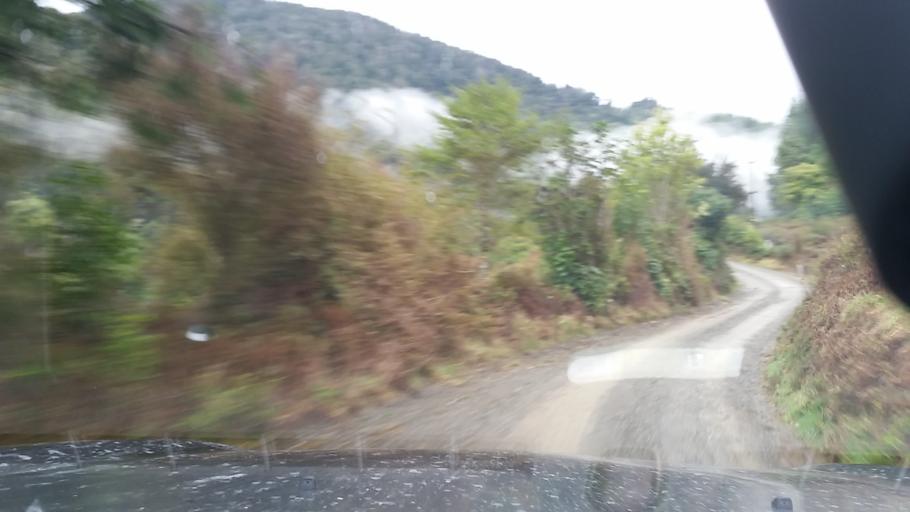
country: NZ
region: Nelson
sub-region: Nelson City
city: Nelson
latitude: -41.3669
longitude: 173.6053
